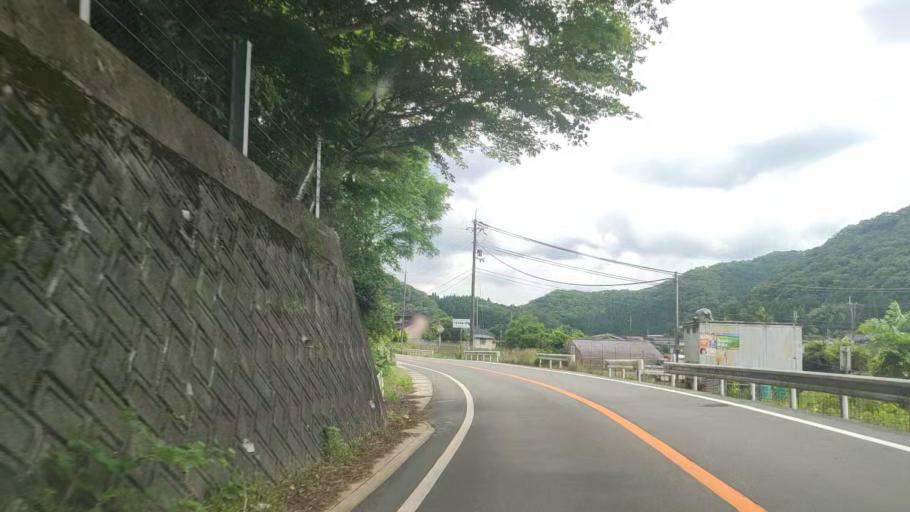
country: JP
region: Hyogo
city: Yamazakicho-nakabirose
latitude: 34.9659
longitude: 134.4479
